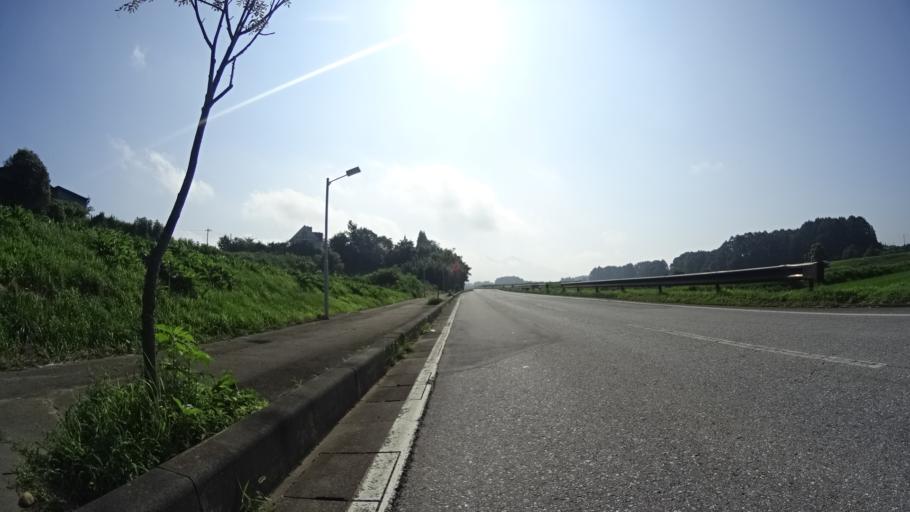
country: JP
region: Nagano
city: Chino
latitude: 35.9658
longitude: 138.2008
